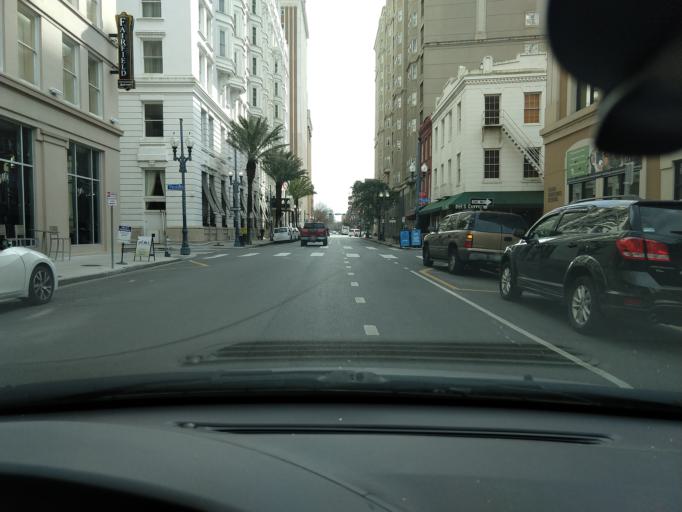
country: US
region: Louisiana
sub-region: Orleans Parish
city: New Orleans
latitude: 29.9513
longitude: -90.0727
